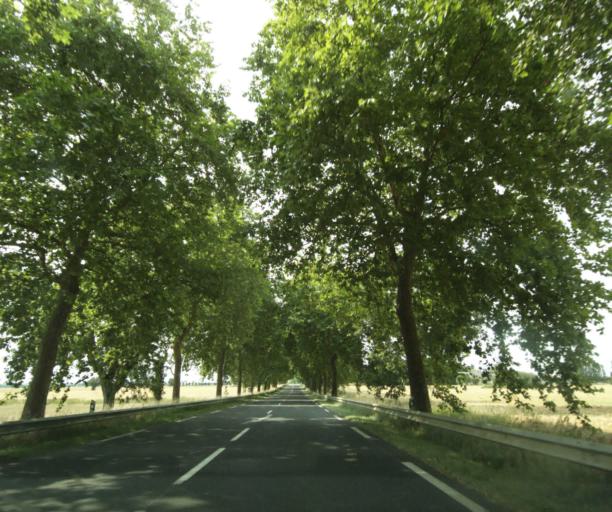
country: FR
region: Centre
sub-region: Departement d'Indre-et-Loire
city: Saint-Paterne-Racan
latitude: 47.5931
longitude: 0.5319
